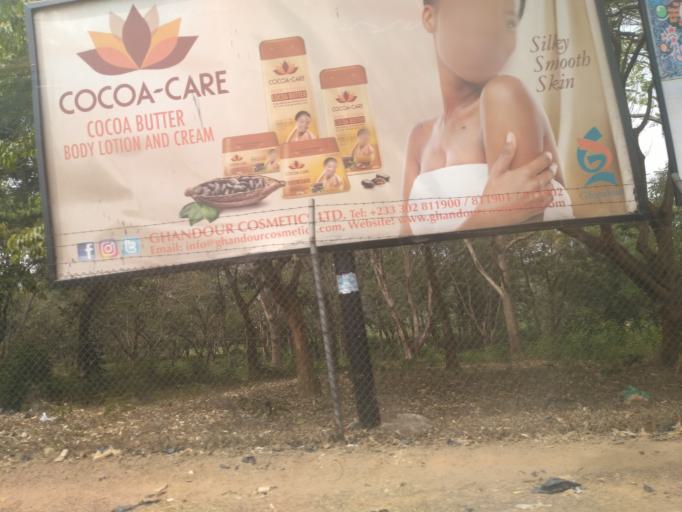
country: GH
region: Ashanti
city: Kumasi
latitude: 6.7059
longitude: -1.6102
